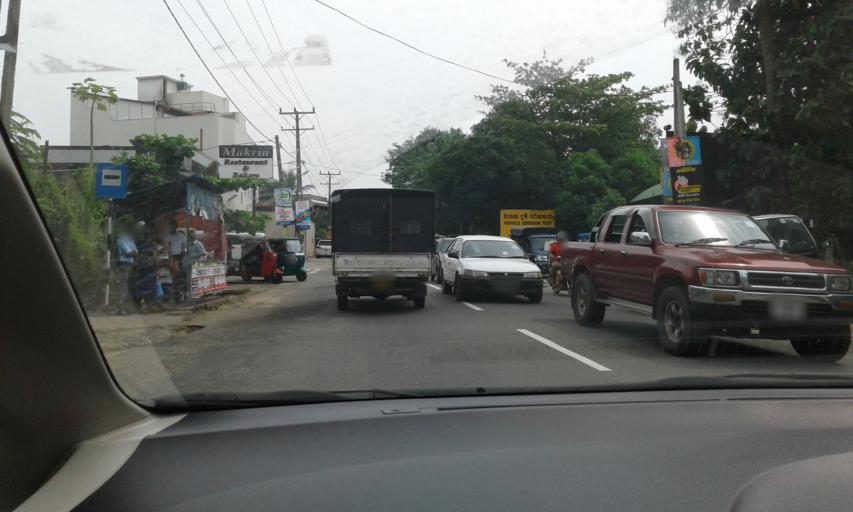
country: LK
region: Western
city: Sri Jayewardenepura Kotte
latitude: 6.8671
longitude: 79.9107
